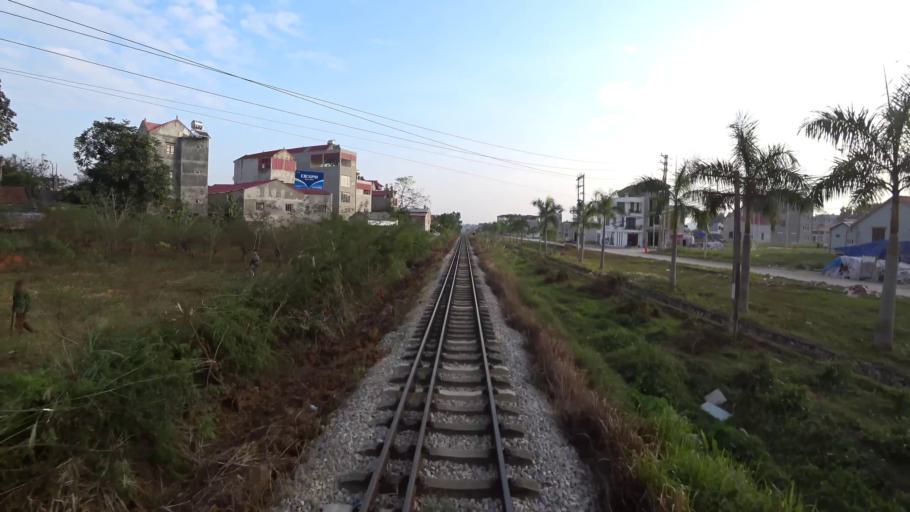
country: VN
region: Lang Son
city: Thi Tran Cao Loc
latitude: 21.8834
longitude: 106.7483
